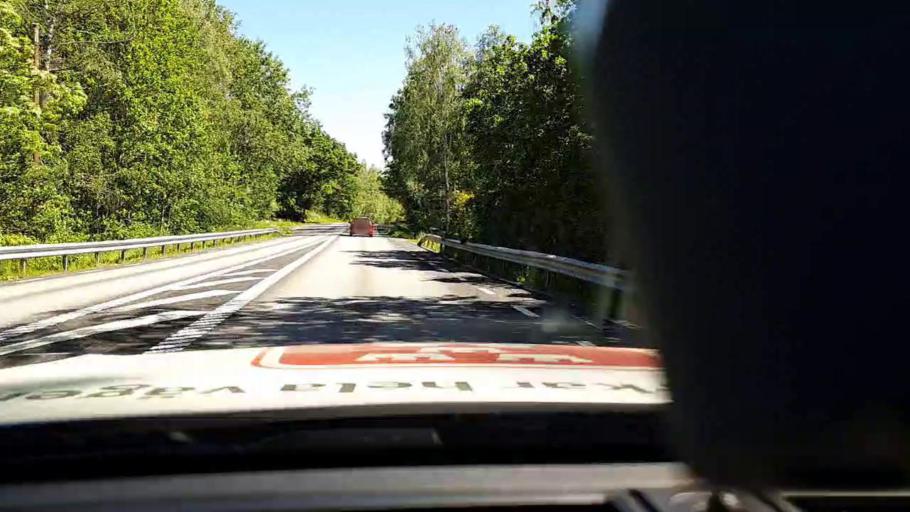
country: SE
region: Uppsala
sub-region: Uppsala Kommun
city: Saevja
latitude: 59.7456
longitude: 17.6558
